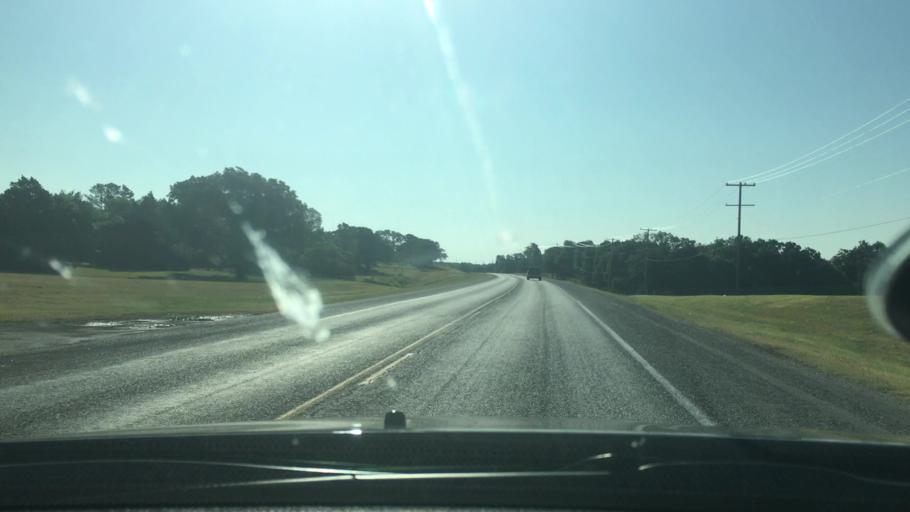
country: US
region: Oklahoma
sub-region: Johnston County
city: Tishomingo
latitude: 34.2372
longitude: -96.7305
